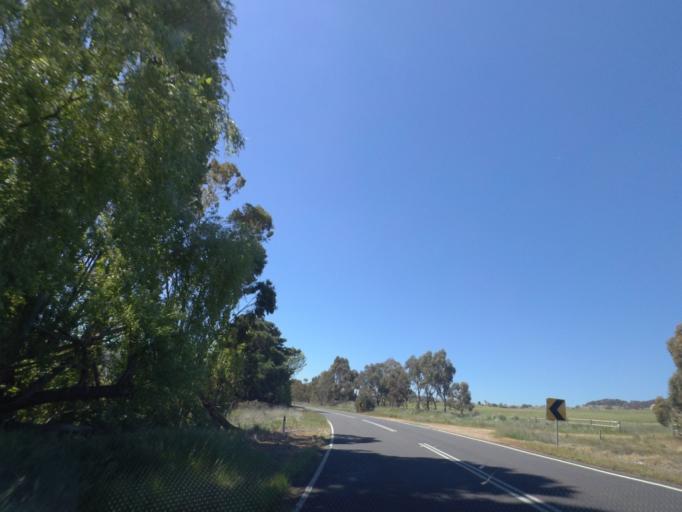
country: AU
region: Victoria
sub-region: Hume
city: Sunbury
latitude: -37.0796
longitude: 144.7686
